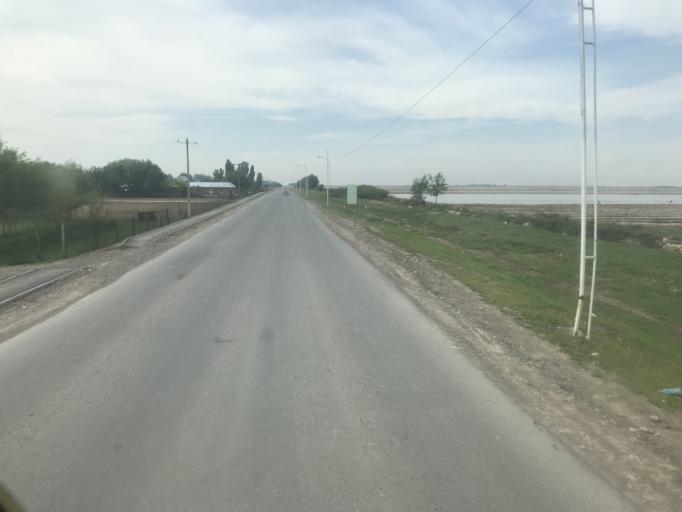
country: KZ
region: Ongtustik Qazaqstan
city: Asykata
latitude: 41.0009
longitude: 68.2133
